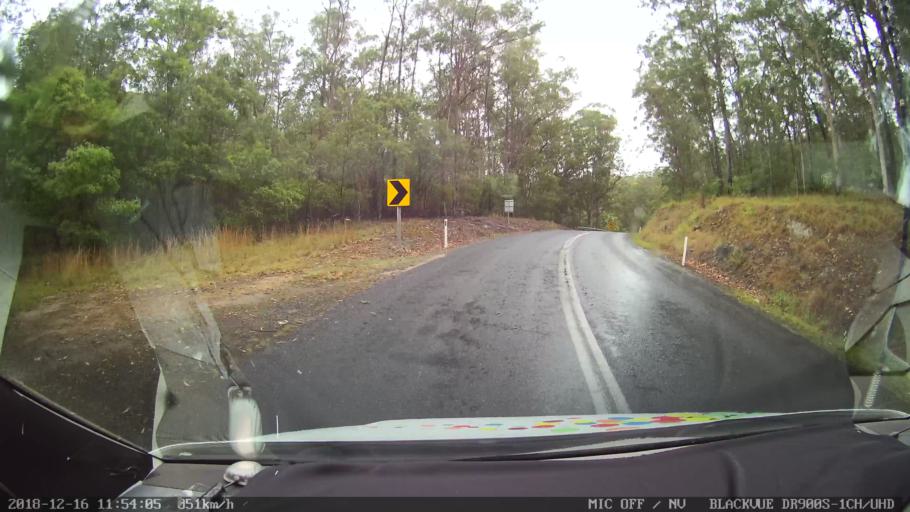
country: AU
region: New South Wales
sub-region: Tenterfield Municipality
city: Carrolls Creek
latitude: -28.9066
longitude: 152.2835
